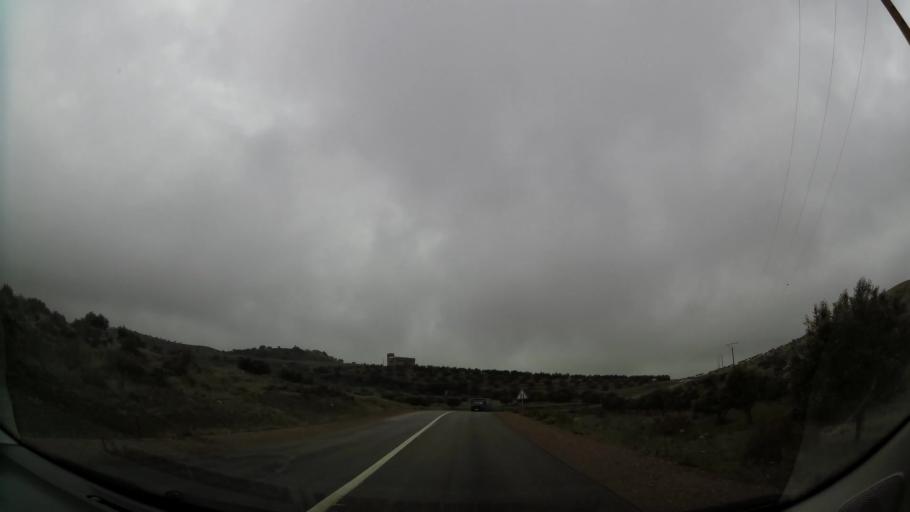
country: MA
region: Oriental
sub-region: Nador
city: Selouane
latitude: 35.1231
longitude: -3.0613
